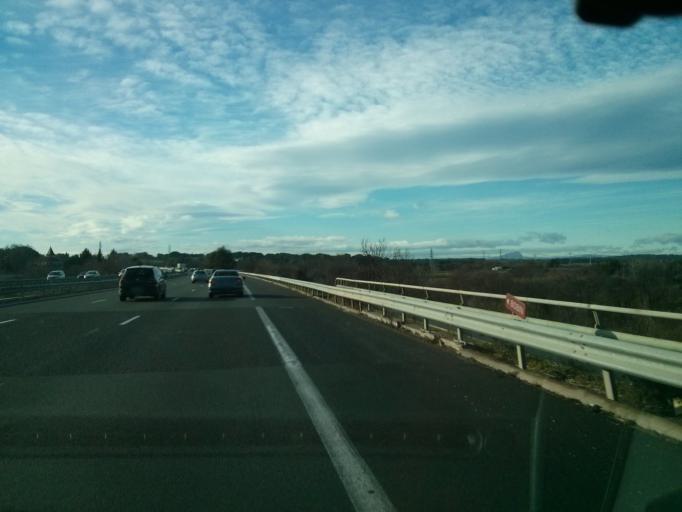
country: FR
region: Languedoc-Roussillon
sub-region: Departement de l'Herault
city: Lunel-Viel
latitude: 43.6969
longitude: 4.0951
